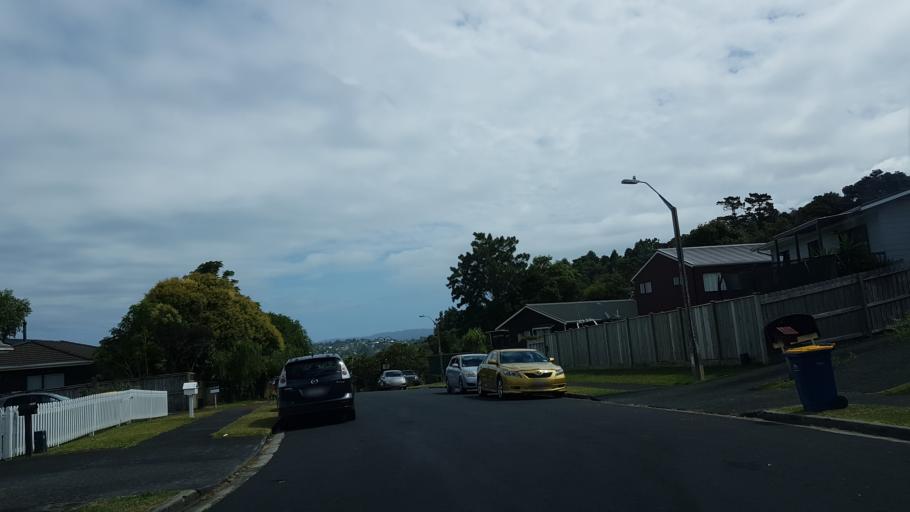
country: NZ
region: Auckland
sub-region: Auckland
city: North Shore
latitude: -36.7808
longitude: 174.7080
